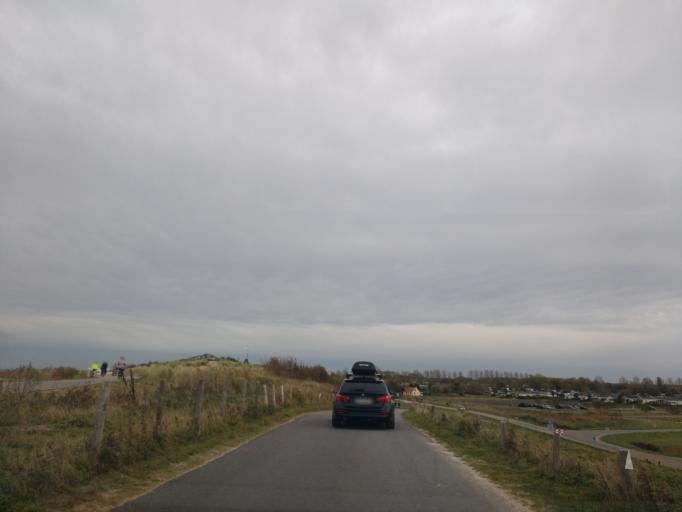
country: NL
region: Zeeland
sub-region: Gemeente Vlissingen
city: Vlissingen
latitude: 51.4058
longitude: 3.5262
